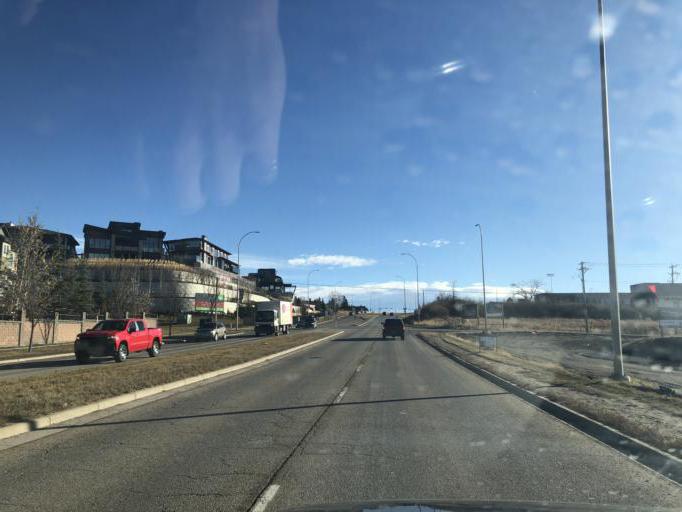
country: CA
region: Alberta
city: Calgary
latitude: 51.0379
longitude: -114.2009
